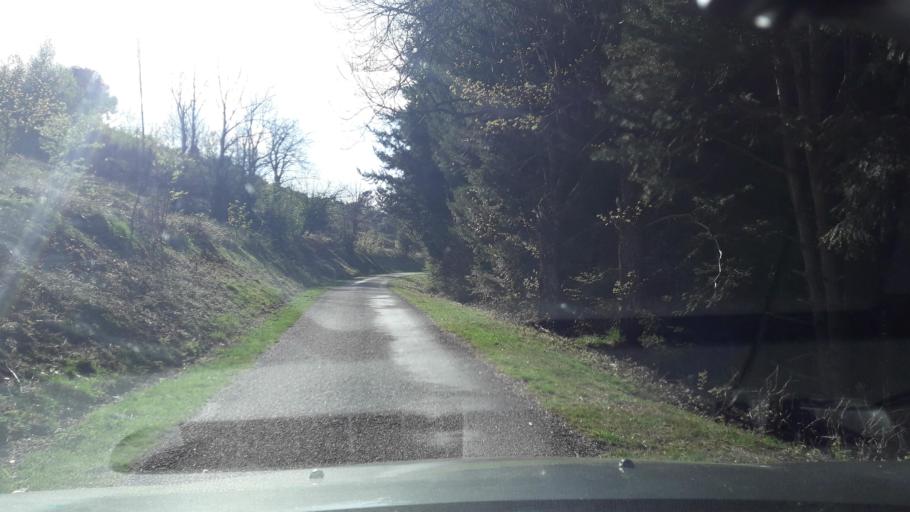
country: FR
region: Languedoc-Roussillon
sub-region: Departement du Gard
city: Valleraugue
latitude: 44.1045
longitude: 3.6590
